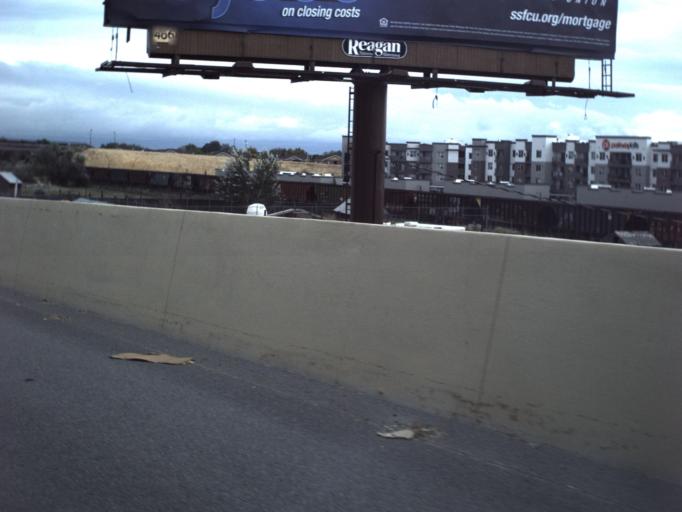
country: US
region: Utah
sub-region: Utah County
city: Orem
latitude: 40.2803
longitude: -111.7237
